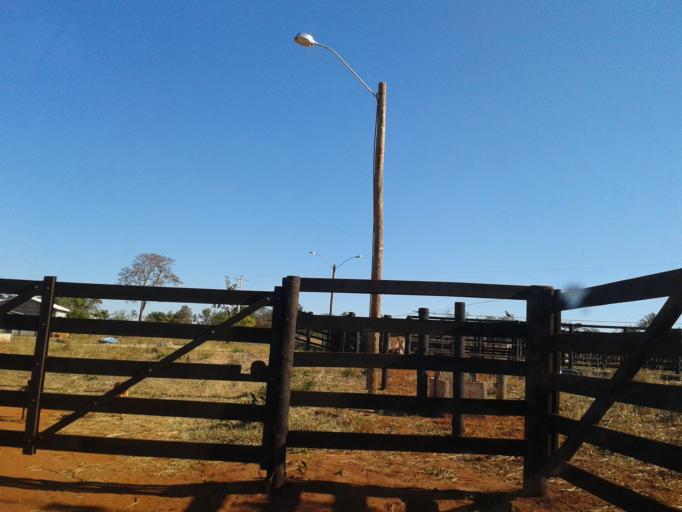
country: BR
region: Minas Gerais
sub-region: Ituiutaba
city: Ituiutaba
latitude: -19.0749
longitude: -49.3332
